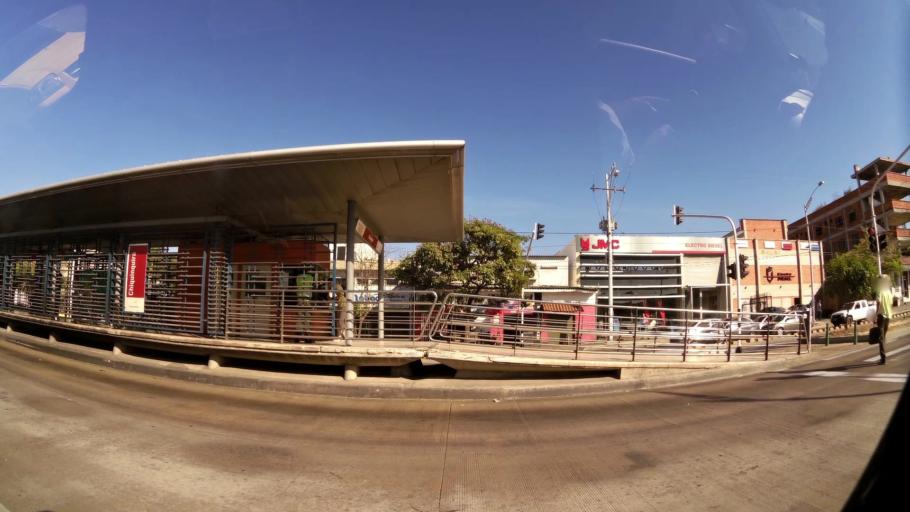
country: CO
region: Atlantico
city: Barranquilla
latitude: 10.9767
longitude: -74.7880
